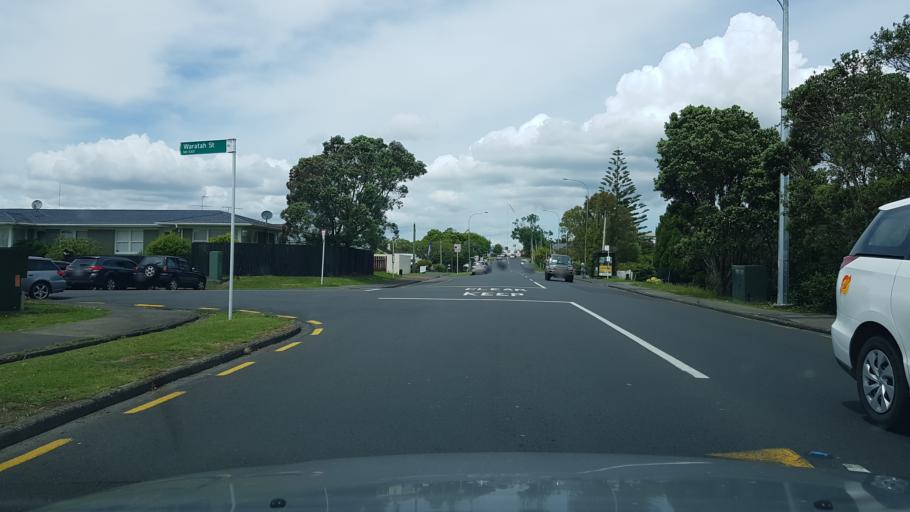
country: NZ
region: Auckland
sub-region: Auckland
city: North Shore
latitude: -36.8065
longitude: 174.7255
